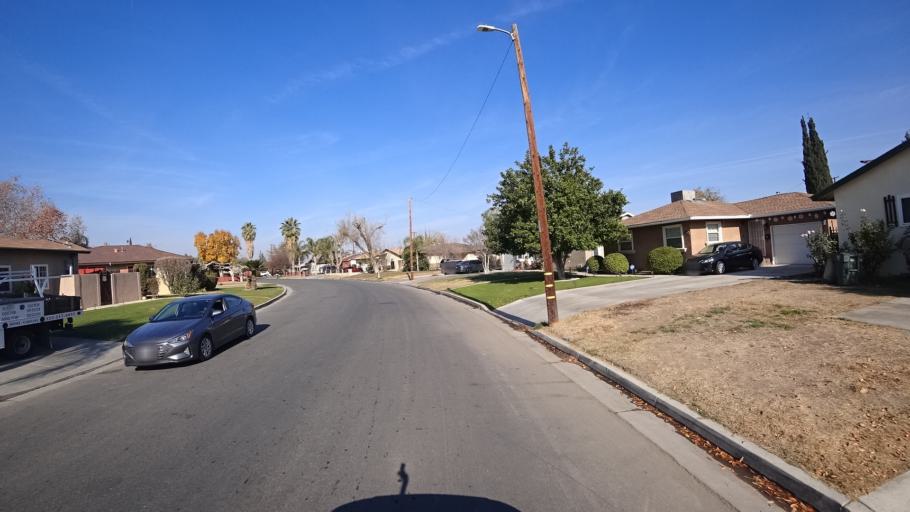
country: US
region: California
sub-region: Kern County
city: Bakersfield
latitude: 35.3295
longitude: -119.0142
